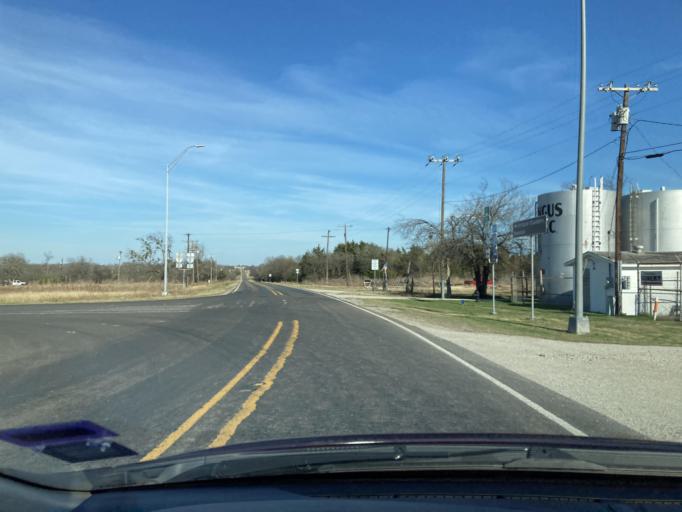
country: US
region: Texas
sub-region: Navarro County
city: Corsicana
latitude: 32.0091
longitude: -96.4330
